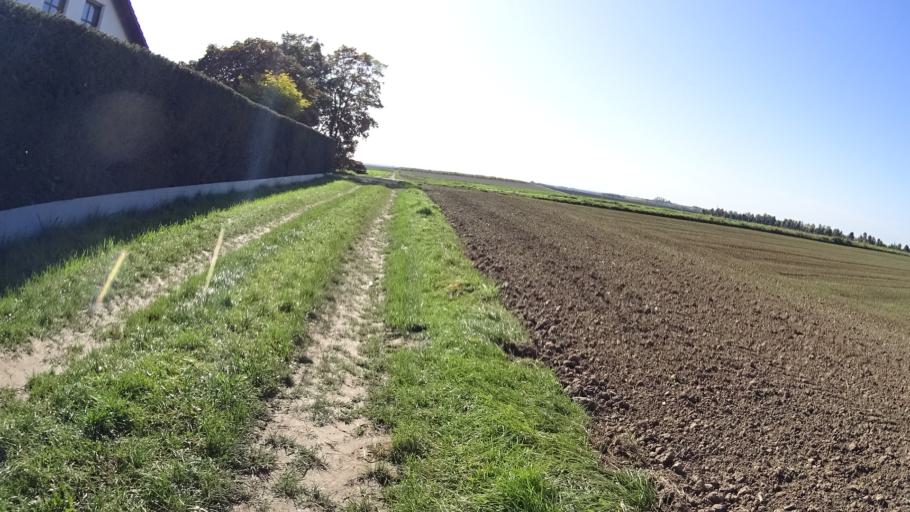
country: DE
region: Bavaria
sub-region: Upper Bavaria
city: Gaimersheim
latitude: 48.8341
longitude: 11.3509
